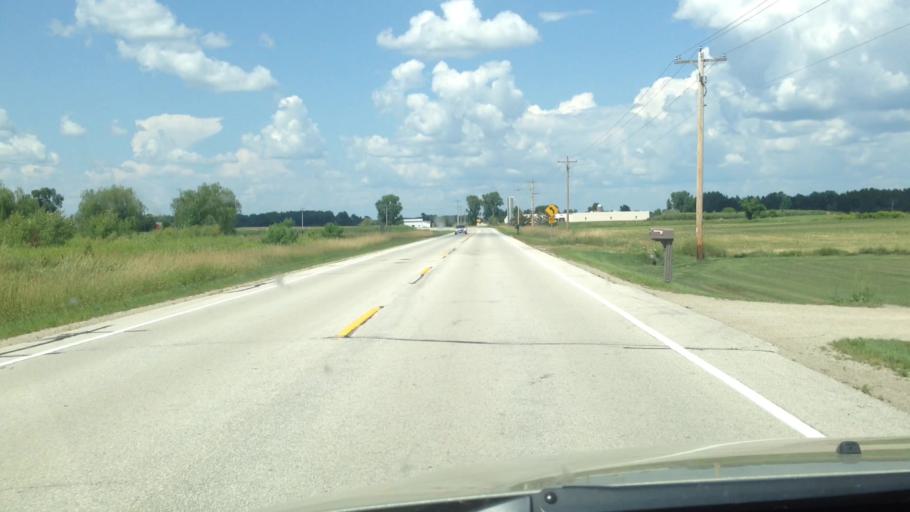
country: US
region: Wisconsin
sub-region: Brown County
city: Pulaski
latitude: 44.6545
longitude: -88.1809
